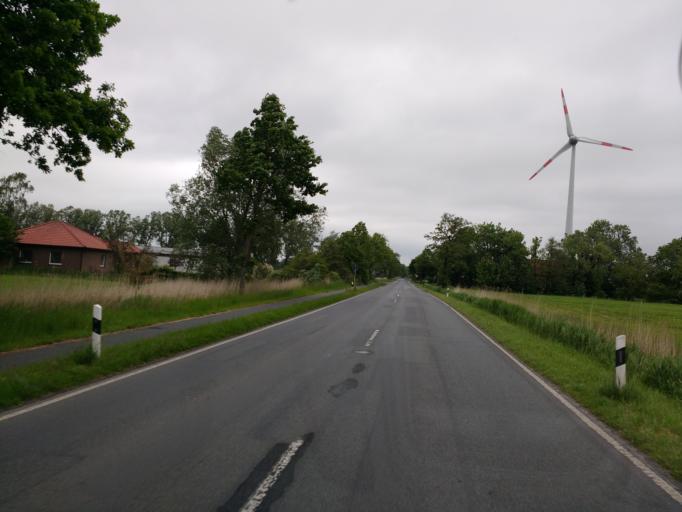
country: DE
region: Lower Saxony
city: Jever
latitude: 53.5903
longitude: 7.9161
